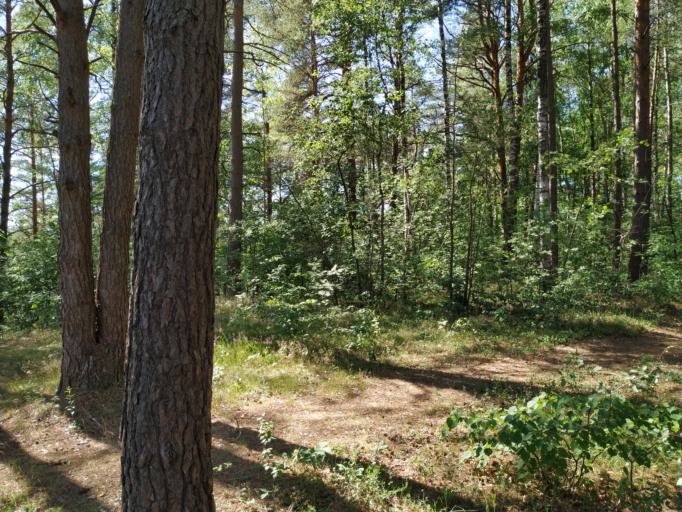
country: LT
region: Vilnius County
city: Rasos
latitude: 54.7605
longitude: 25.3468
